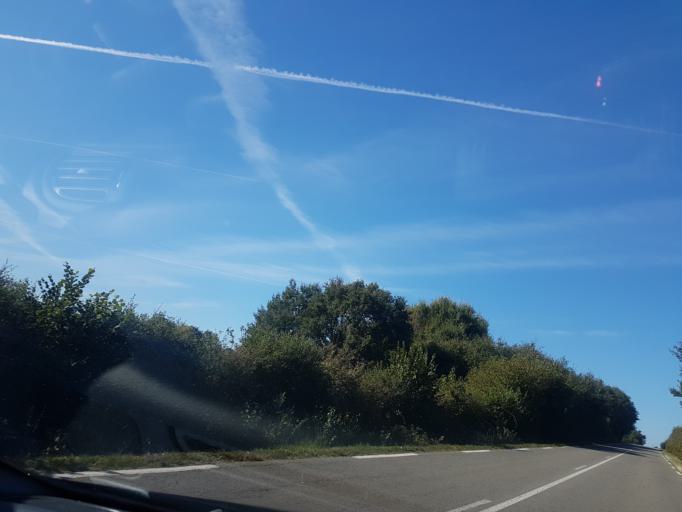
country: FR
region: Pays de la Loire
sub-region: Departement de la Loire-Atlantique
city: Casson
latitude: 47.4284
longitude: -1.5693
